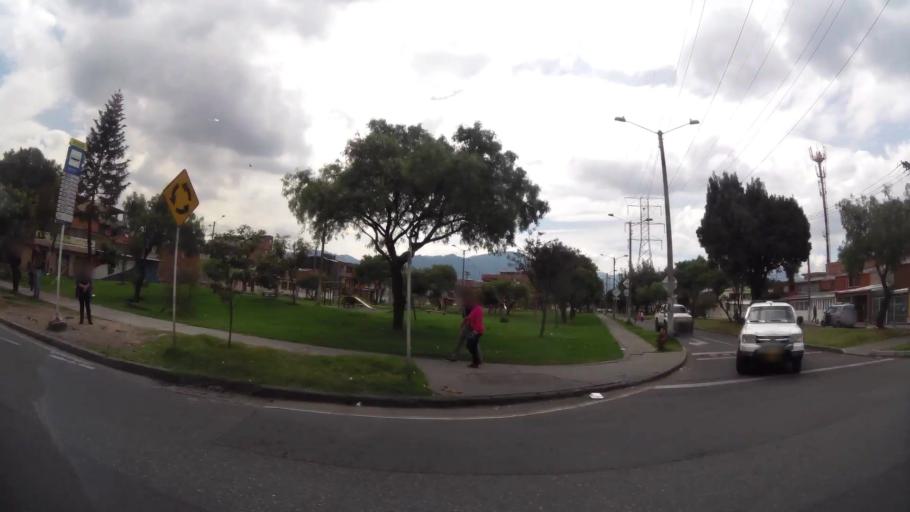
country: CO
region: Bogota D.C.
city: Bogota
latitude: 4.6138
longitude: -74.1151
